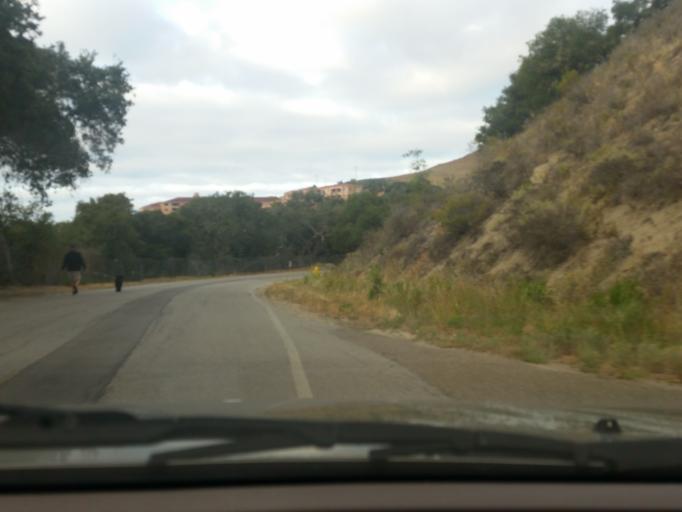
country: US
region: California
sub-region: San Luis Obispo County
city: Avila Beach
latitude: 35.1822
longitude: -120.7372
